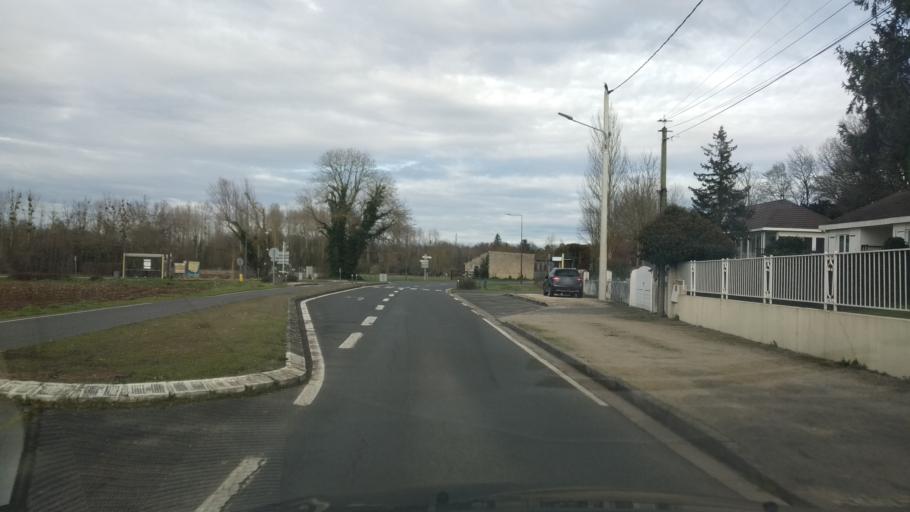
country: FR
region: Poitou-Charentes
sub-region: Departement de la Vienne
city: Chasseneuil-du-Poitou
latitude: 46.6464
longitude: 0.3824
